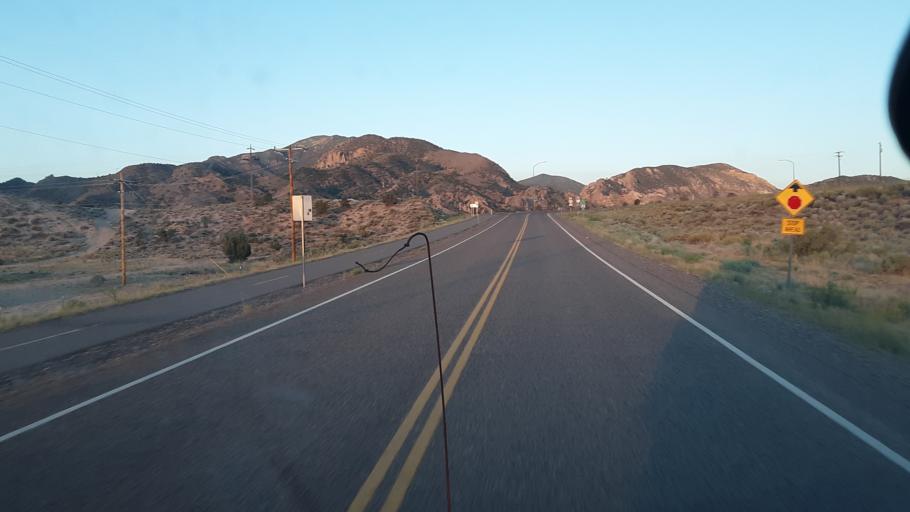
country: US
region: Utah
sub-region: Sevier County
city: Monroe
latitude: 38.5904
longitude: -112.2562
